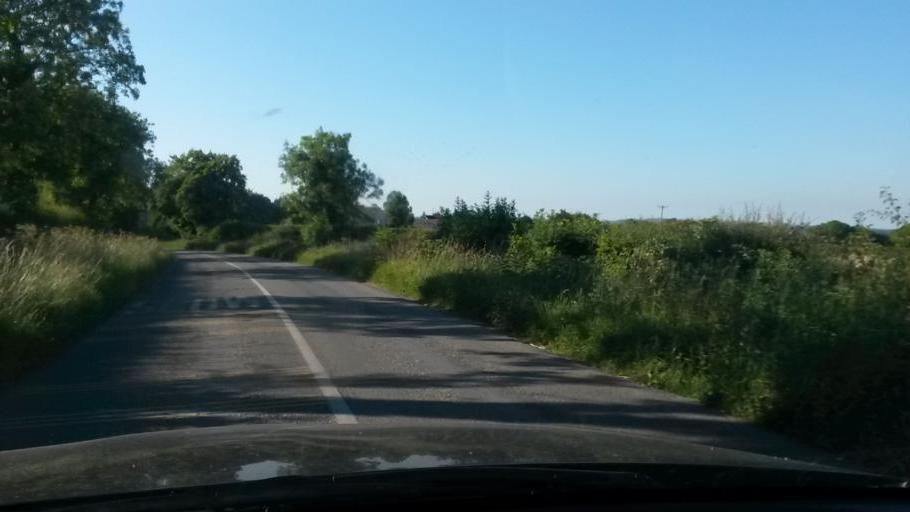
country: IE
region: Leinster
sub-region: Dublin City
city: Finglas
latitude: 53.4715
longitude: -6.3193
